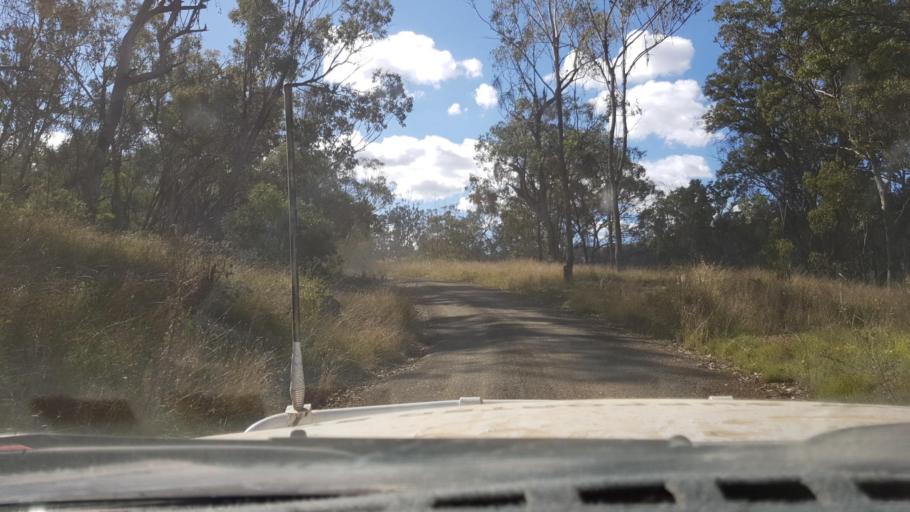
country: AU
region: New South Wales
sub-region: Tamworth Municipality
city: Manilla
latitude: -30.4797
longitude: 150.7703
